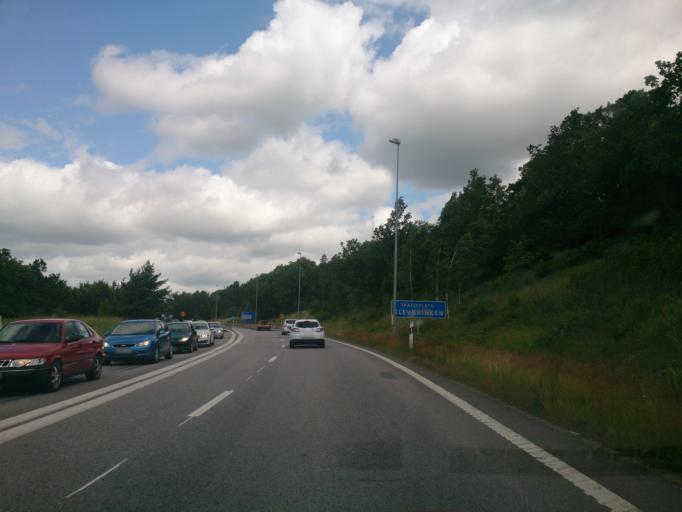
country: SE
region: OEstergoetland
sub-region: Soderkopings Kommun
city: Soederkoeping
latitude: 58.4896
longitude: 16.3098
